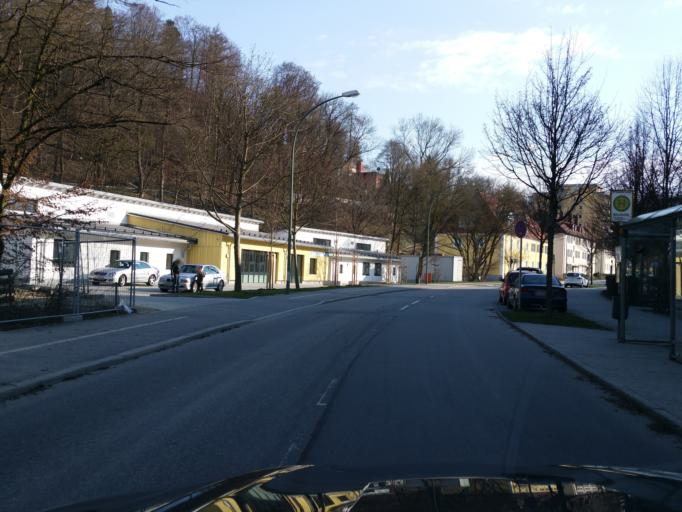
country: DE
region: Bavaria
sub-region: Lower Bavaria
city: Landshut
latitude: 48.5411
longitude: 12.1672
